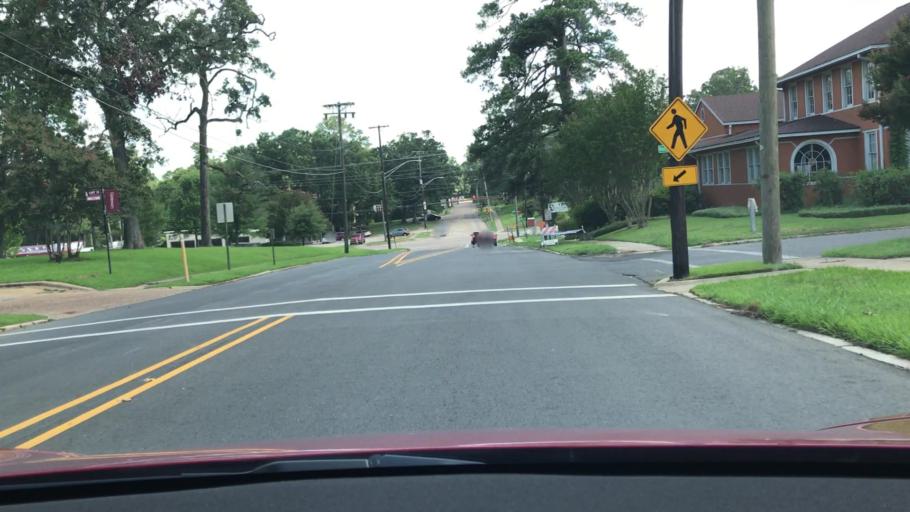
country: US
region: Louisiana
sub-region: Bossier Parish
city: Bossier City
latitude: 32.4830
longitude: -93.7339
